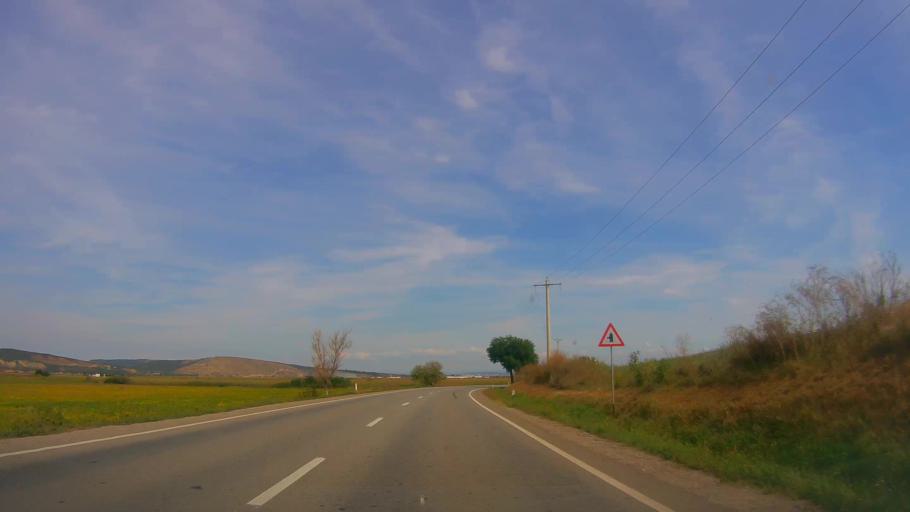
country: RO
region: Mures
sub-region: Comuna Sanpaul
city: Valea Izvoarelor
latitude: 46.4544
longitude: 24.3782
